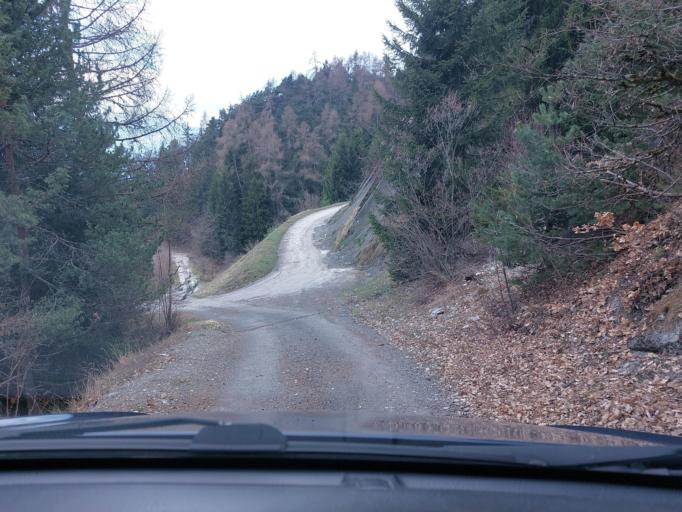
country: CH
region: Valais
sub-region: Sion District
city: Saviese
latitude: 46.2711
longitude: 7.3176
